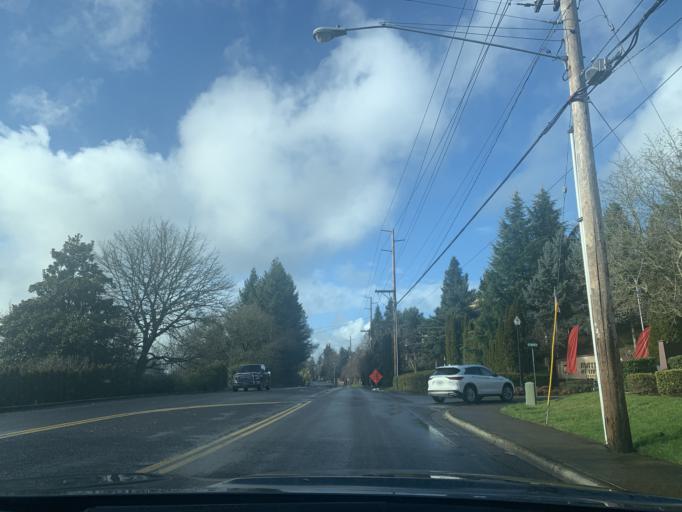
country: US
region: Oregon
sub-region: Washington County
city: King City
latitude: 45.4035
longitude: -122.8189
